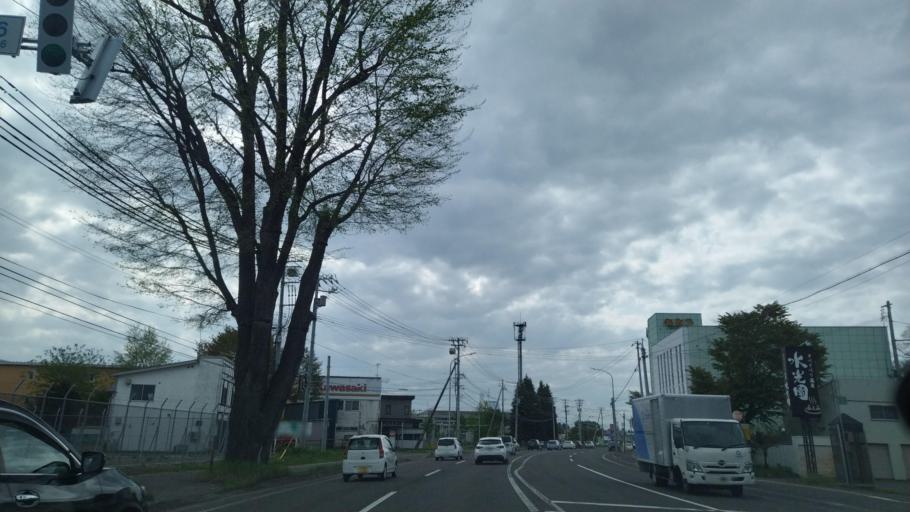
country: JP
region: Hokkaido
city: Obihiro
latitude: 42.9269
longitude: 143.2228
